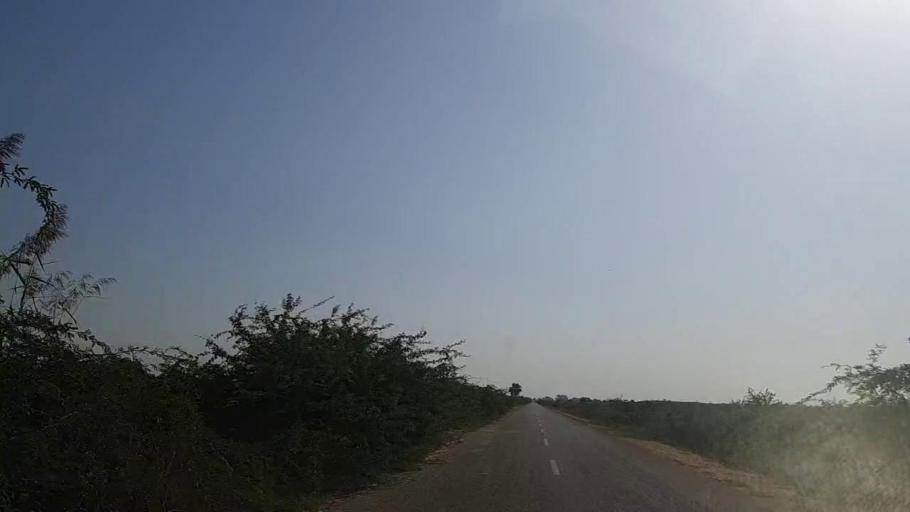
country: PK
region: Sindh
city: Jati
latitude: 24.4384
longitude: 68.2608
